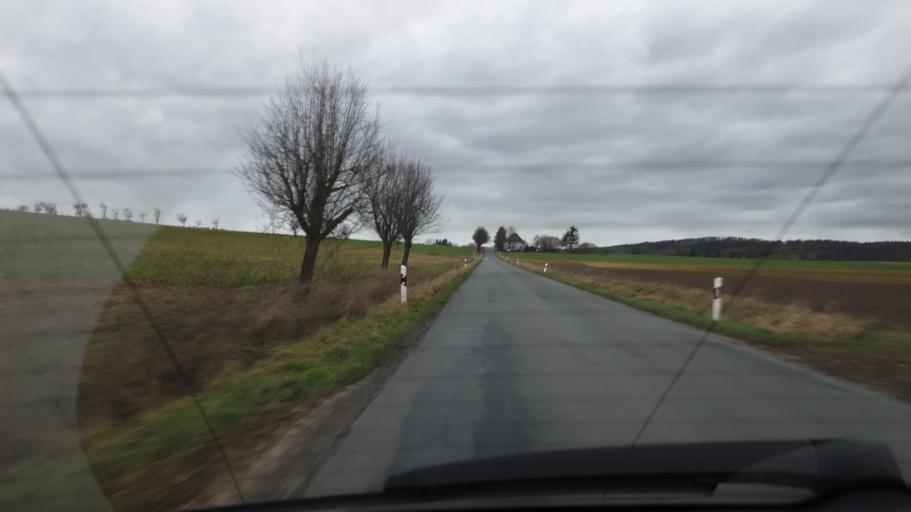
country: DE
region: North Rhine-Westphalia
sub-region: Regierungsbezirk Detmold
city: Lemgo
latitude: 52.0423
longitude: 8.8501
